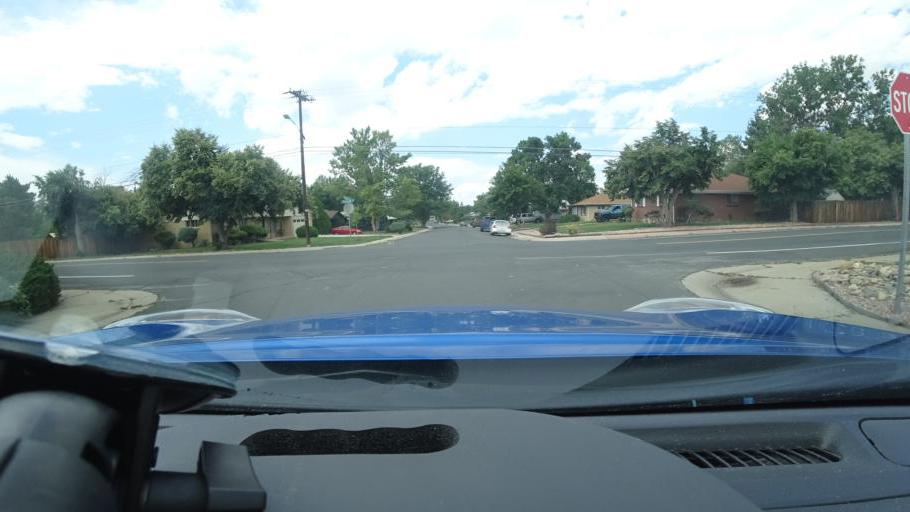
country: US
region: Colorado
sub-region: Adams County
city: Aurora
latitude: 39.7219
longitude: -104.8364
